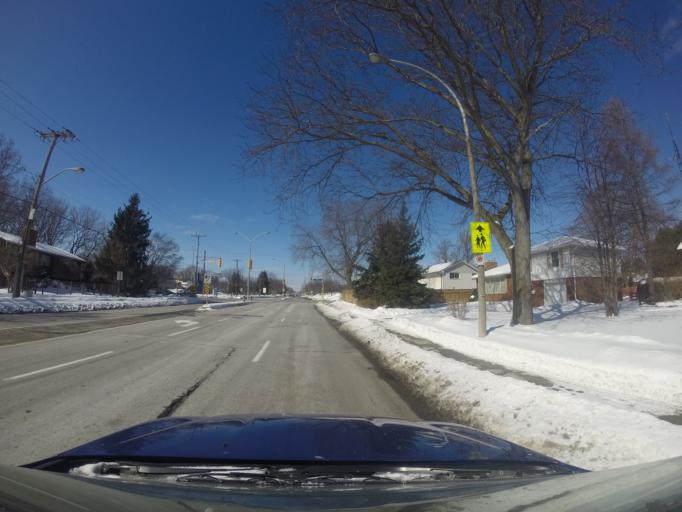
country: CA
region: Ontario
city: Burlington
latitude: 43.3523
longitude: -79.7688
